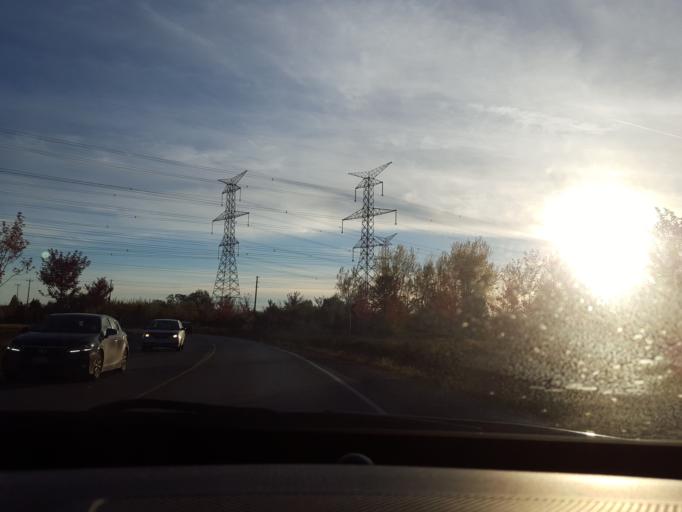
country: CA
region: Ontario
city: Markham
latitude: 43.8502
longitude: -79.2262
